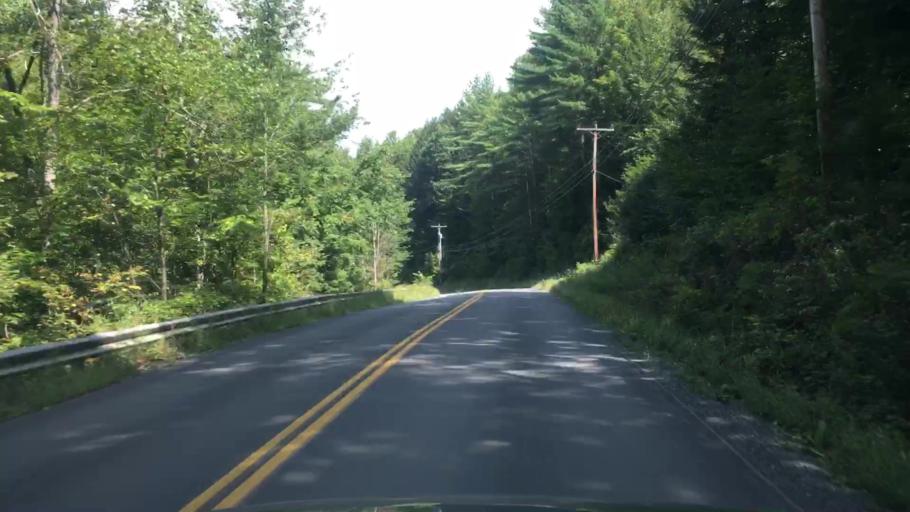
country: US
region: Vermont
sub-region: Windham County
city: West Brattleboro
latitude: 42.8002
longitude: -72.6196
